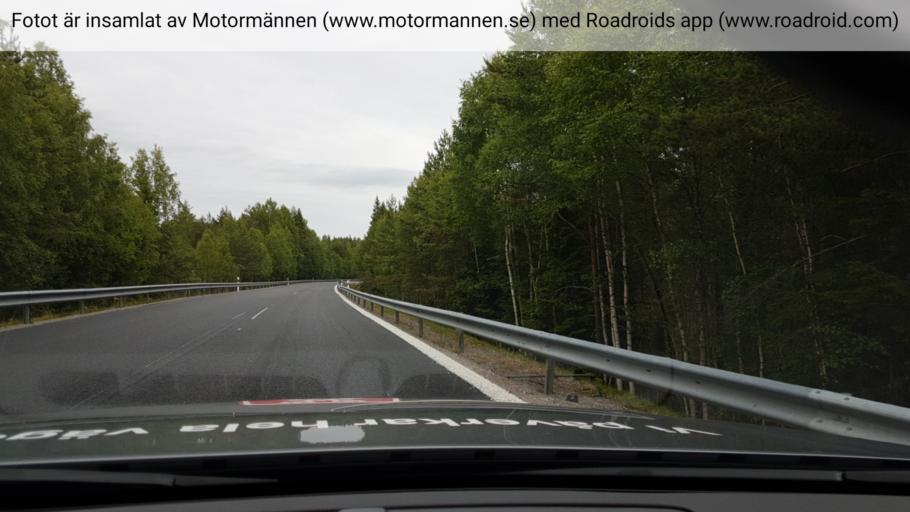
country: SE
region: Vaestmanland
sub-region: Skinnskattebergs Kommun
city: Skinnskatteberg
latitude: 59.8598
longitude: 15.5918
